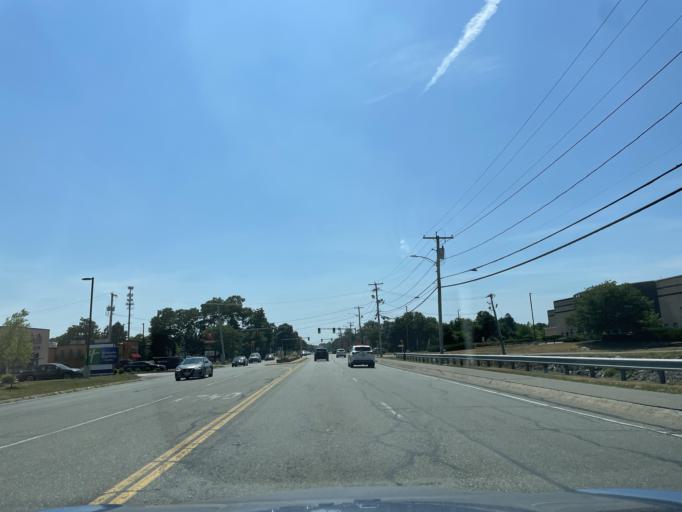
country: US
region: Massachusetts
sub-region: Norfolk County
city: Randolph
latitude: 42.1634
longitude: -71.0599
